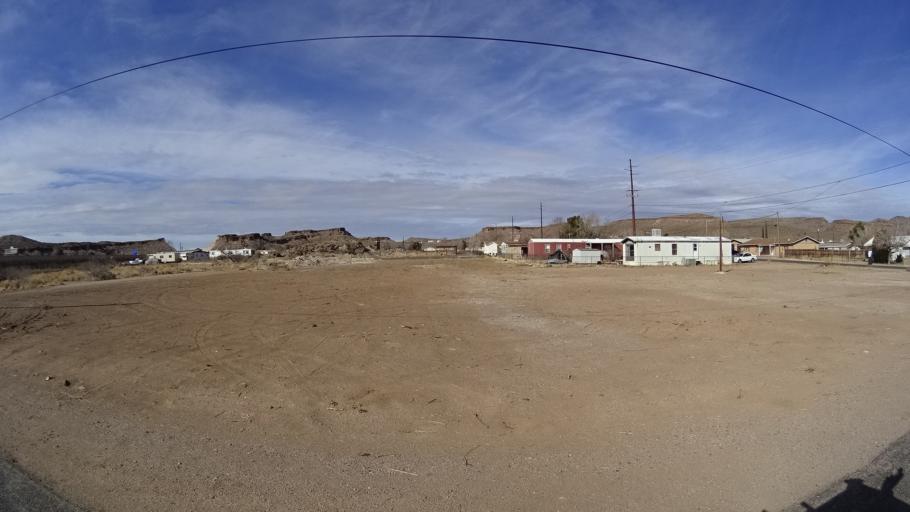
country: US
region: Arizona
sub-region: Mohave County
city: Kingman
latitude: 35.2166
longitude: -114.0445
